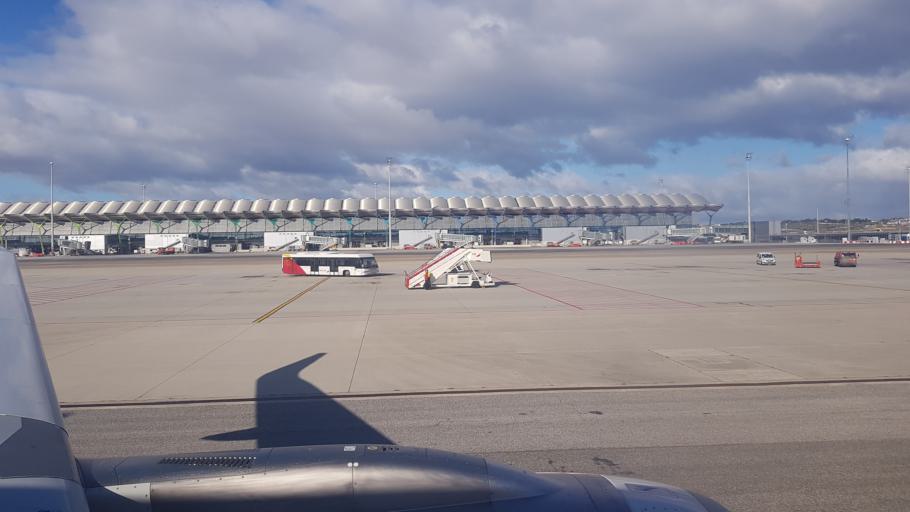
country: ES
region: Madrid
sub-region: Provincia de Madrid
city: Barajas de Madrid
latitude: 40.4951
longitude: -3.5864
